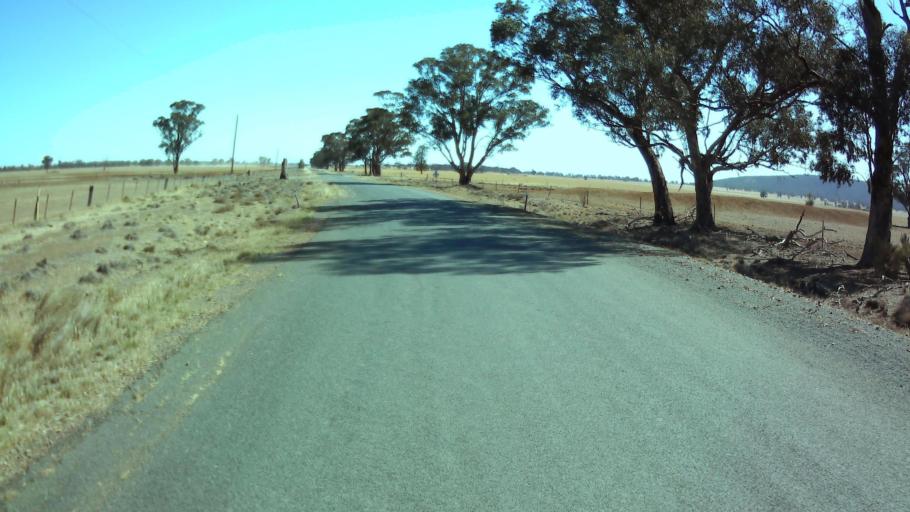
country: AU
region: New South Wales
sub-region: Weddin
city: Grenfell
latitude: -33.7047
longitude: 147.9183
